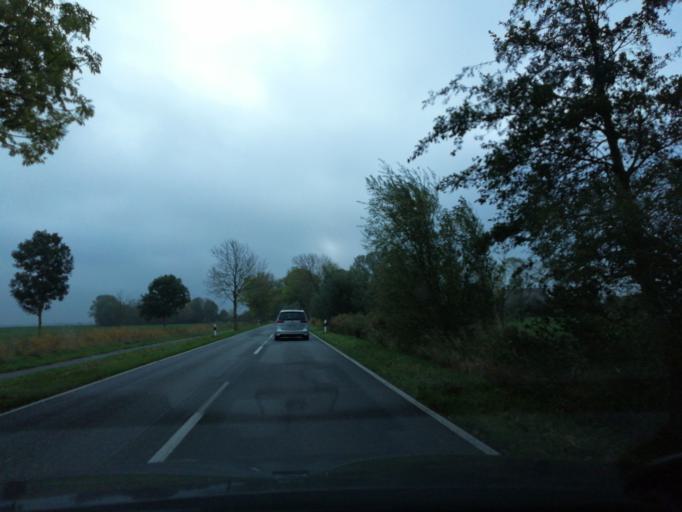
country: DE
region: Lower Saxony
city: Jever
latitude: 53.6812
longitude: 7.8618
